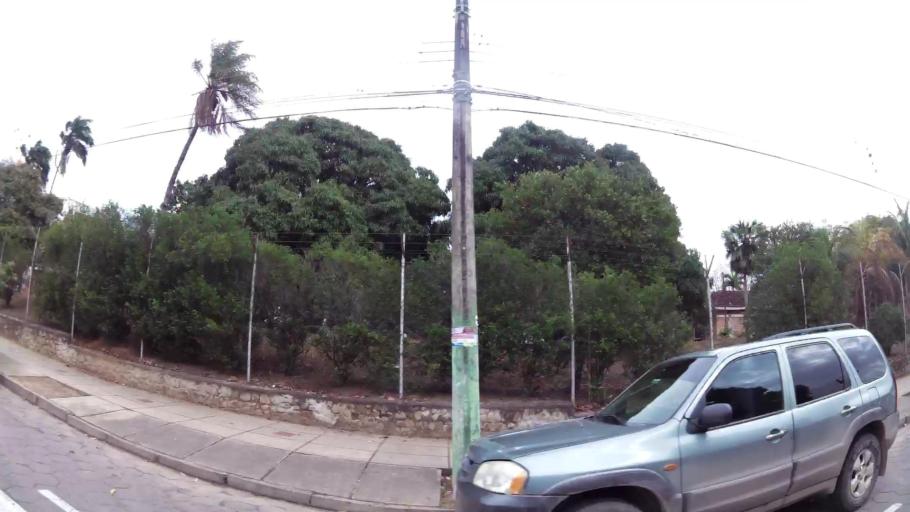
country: BO
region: Santa Cruz
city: Santa Cruz de la Sierra
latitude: -17.7691
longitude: -63.1854
